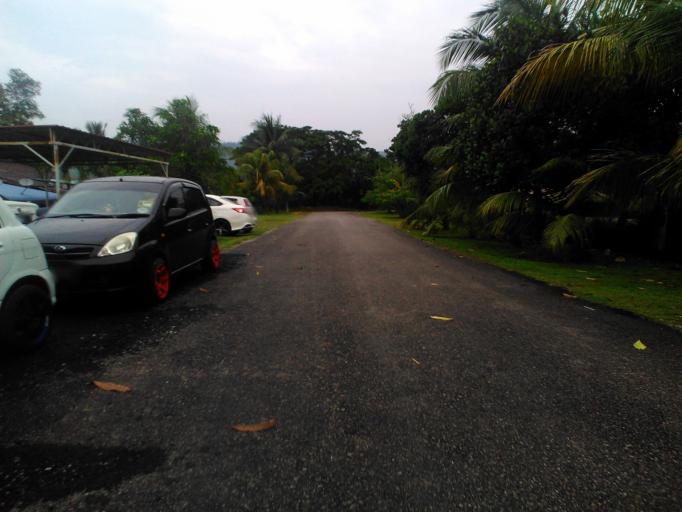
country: MY
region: Kedah
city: Kulim
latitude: 5.3618
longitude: 100.5787
